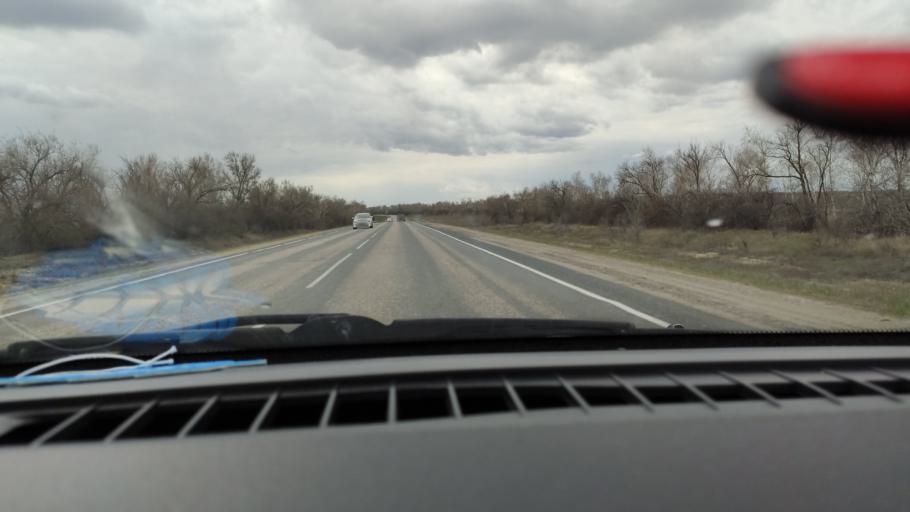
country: RU
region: Saratov
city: Sinodskoye
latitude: 51.9543
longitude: 46.6127
